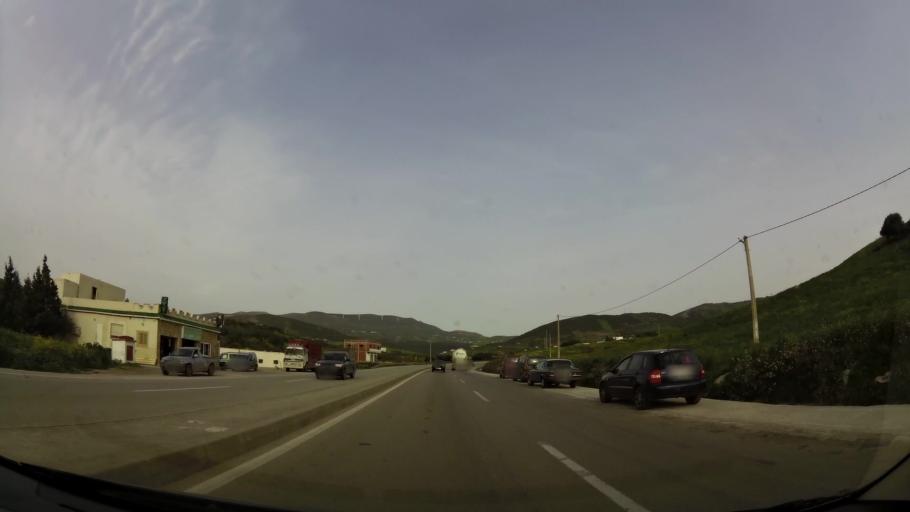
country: MA
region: Tanger-Tetouan
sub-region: Tanger-Assilah
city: Dar Chaoui
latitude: 35.5681
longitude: -5.6125
